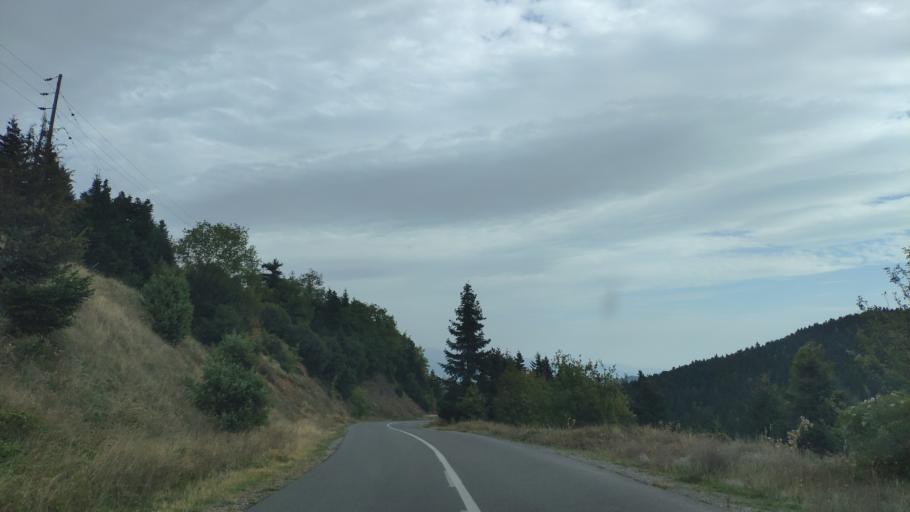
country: GR
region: Central Greece
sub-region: Nomos Fthiotidos
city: Stavros
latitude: 38.7258
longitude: 22.3354
